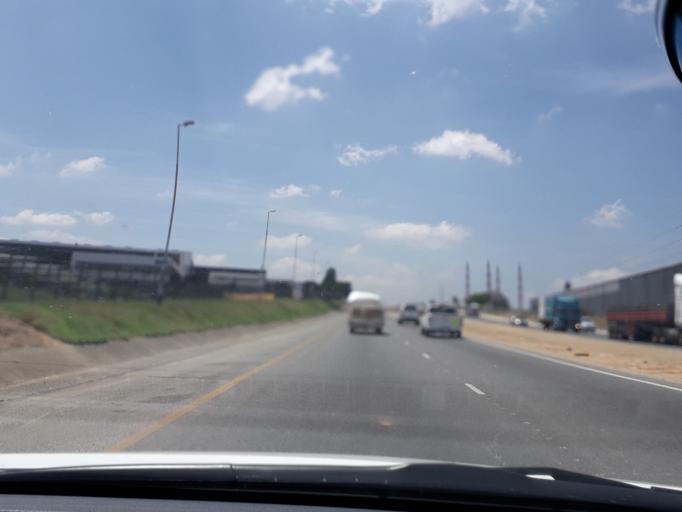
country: ZA
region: Gauteng
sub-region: City of Johannesburg Metropolitan Municipality
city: Midrand
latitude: -26.0183
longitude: 28.1233
